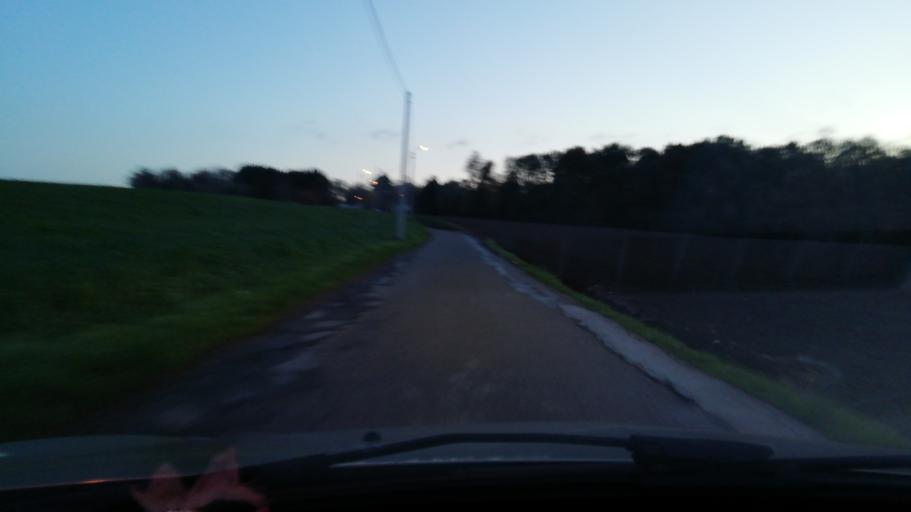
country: FR
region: Nord-Pas-de-Calais
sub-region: Departement du Nord
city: Marpent
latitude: 50.2808
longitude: 4.0895
